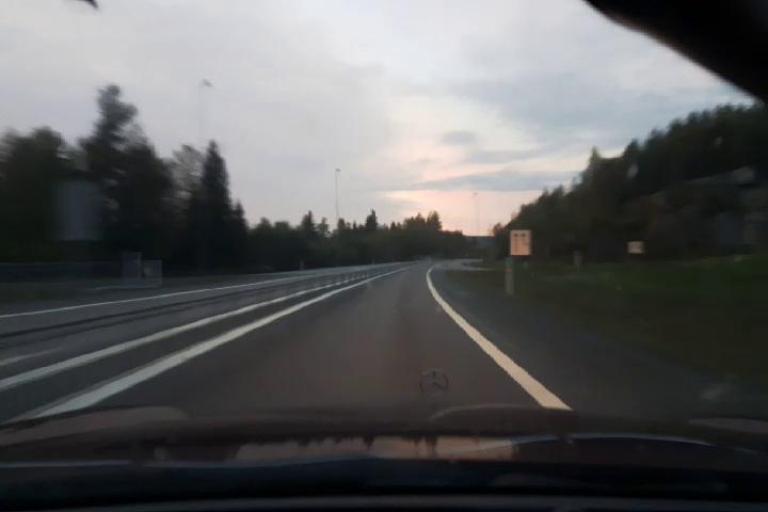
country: SE
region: Vaesternorrland
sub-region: Kramfors Kommun
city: Nordingra
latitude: 62.9401
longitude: 18.0939
